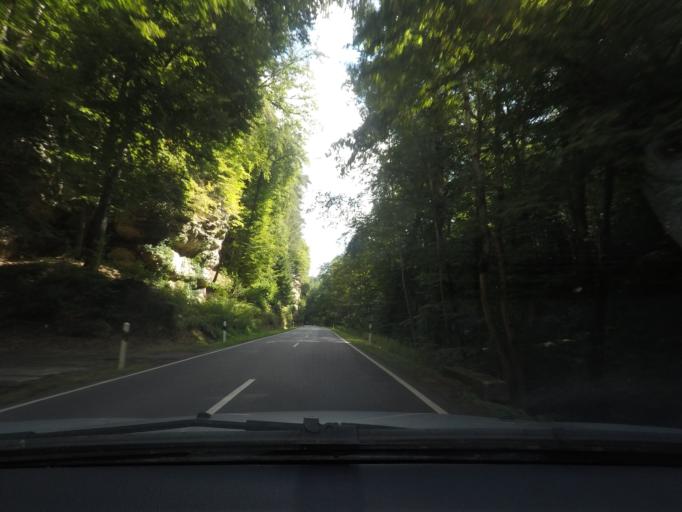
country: LU
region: Grevenmacher
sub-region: Canton d'Echternach
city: Waldbillig
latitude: 49.7742
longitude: 6.2882
